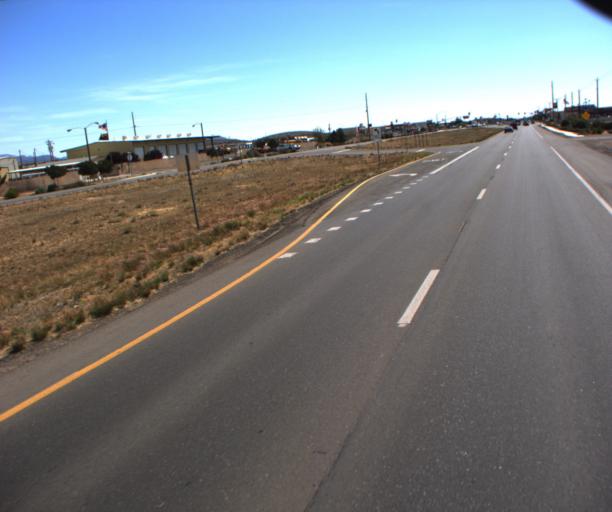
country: US
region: Arizona
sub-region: Mohave County
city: New Kingman-Butler
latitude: 35.2273
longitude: -114.0013
